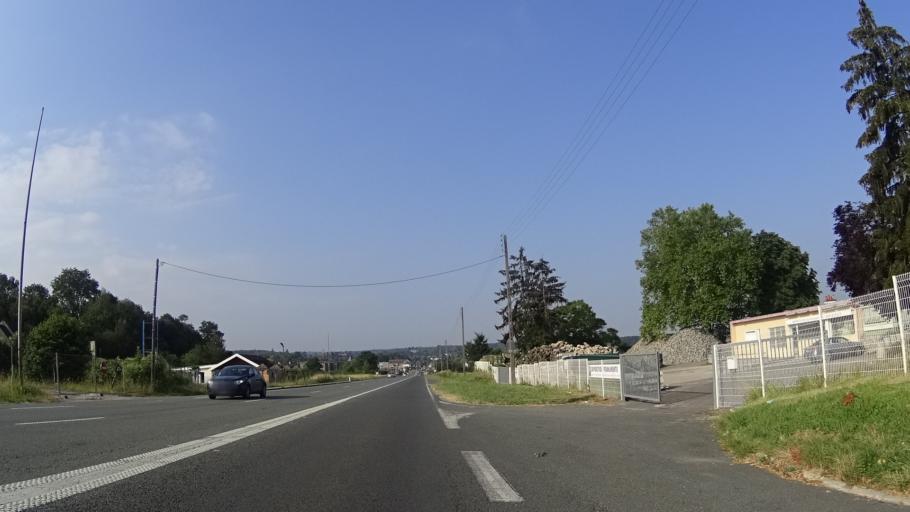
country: FR
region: Ile-de-France
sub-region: Departement du Val-d'Oise
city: Chaumontel
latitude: 49.1317
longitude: 2.4335
